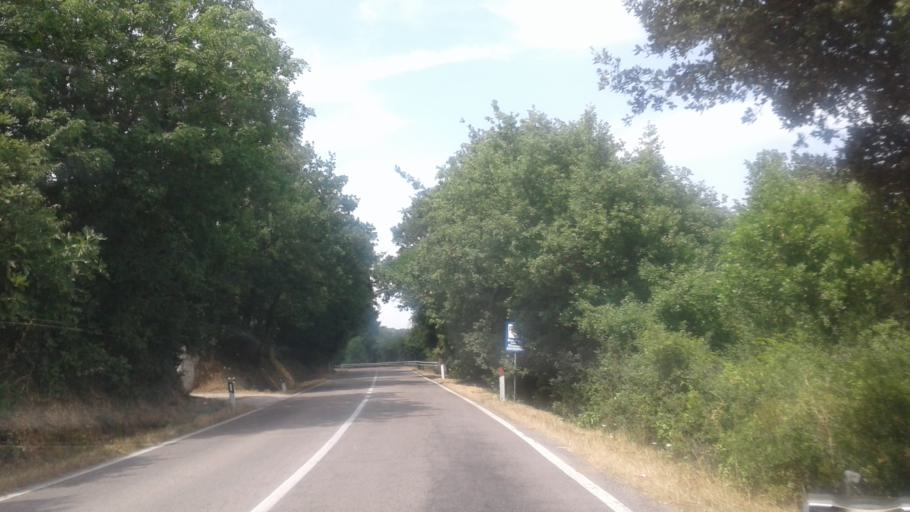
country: IT
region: Sardinia
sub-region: Provincia di Olbia-Tempio
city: Tempio Pausania
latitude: 40.9096
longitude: 9.0835
